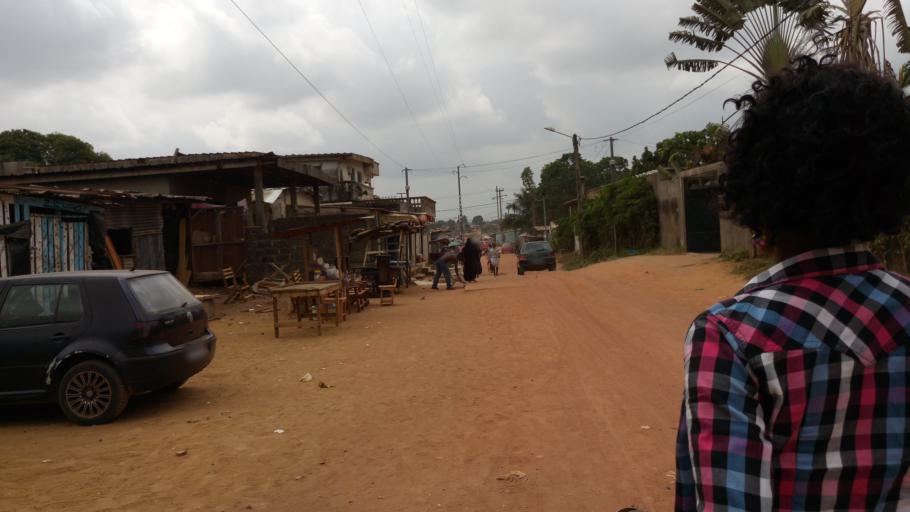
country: CI
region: Lagunes
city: Abobo
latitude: 5.4138
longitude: -4.0003
